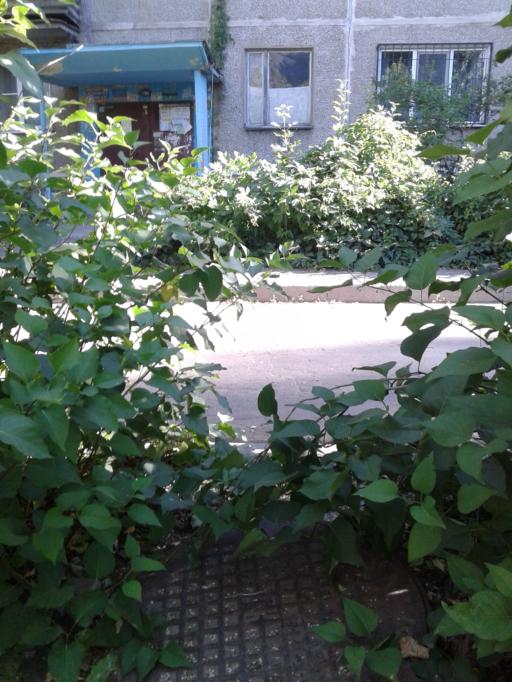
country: RU
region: Voronezj
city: Pridonskoy
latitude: 51.6555
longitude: 39.1153
